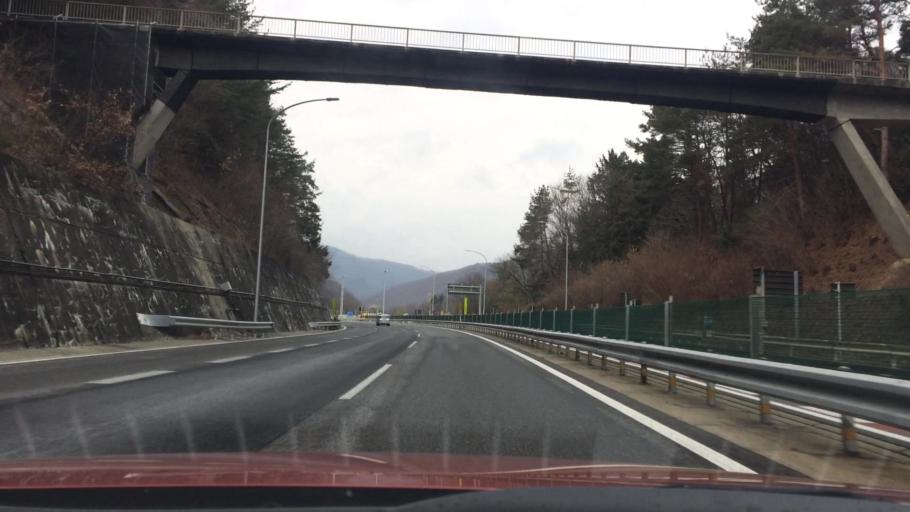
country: JP
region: Nagano
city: Iida
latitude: 35.4486
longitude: 137.7165
